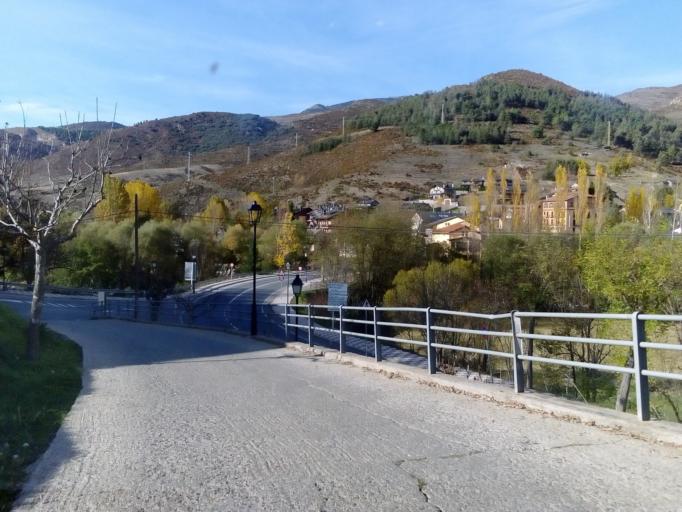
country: ES
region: Catalonia
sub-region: Provincia de Lleida
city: Bellver de Cerdanya
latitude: 42.3711
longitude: 1.7763
